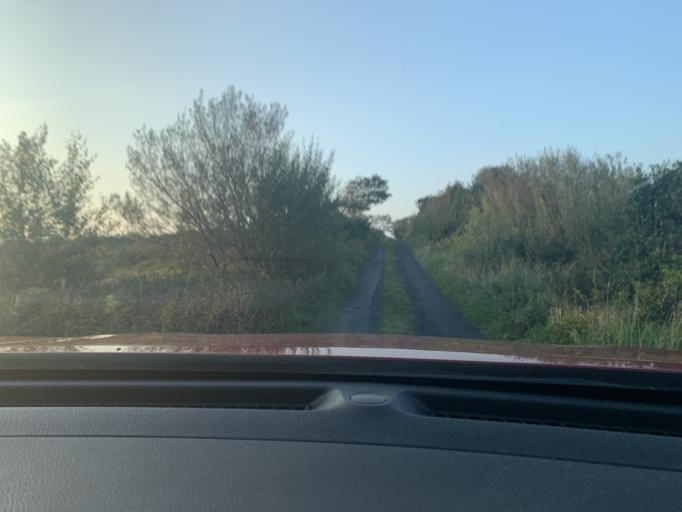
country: IE
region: Connaught
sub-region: County Leitrim
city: Kinlough
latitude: 54.4561
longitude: -8.3981
